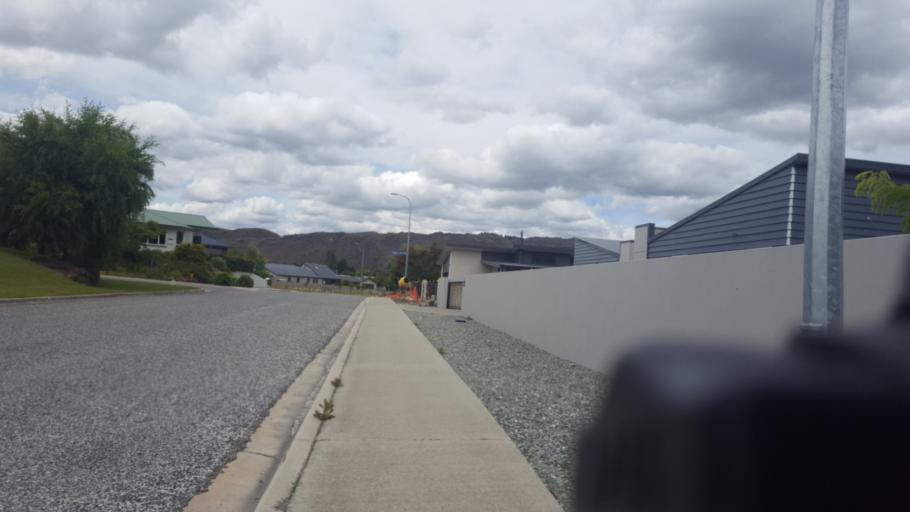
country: NZ
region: Otago
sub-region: Queenstown-Lakes District
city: Wanaka
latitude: -45.2537
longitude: 169.3822
